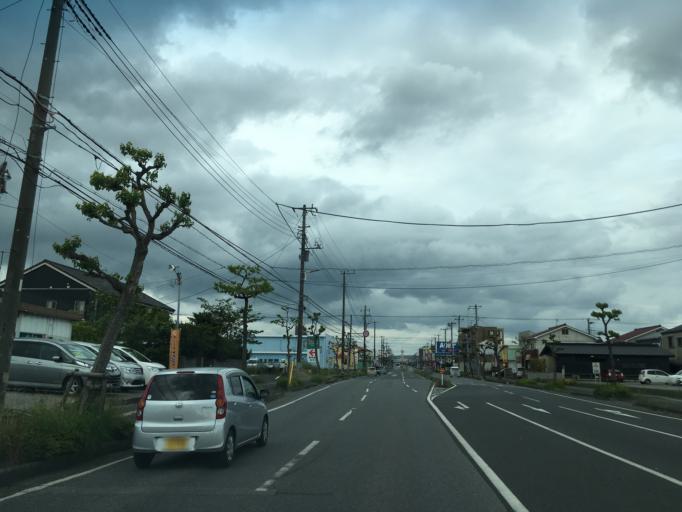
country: JP
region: Chiba
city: Kimitsu
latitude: 35.3328
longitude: 139.8868
